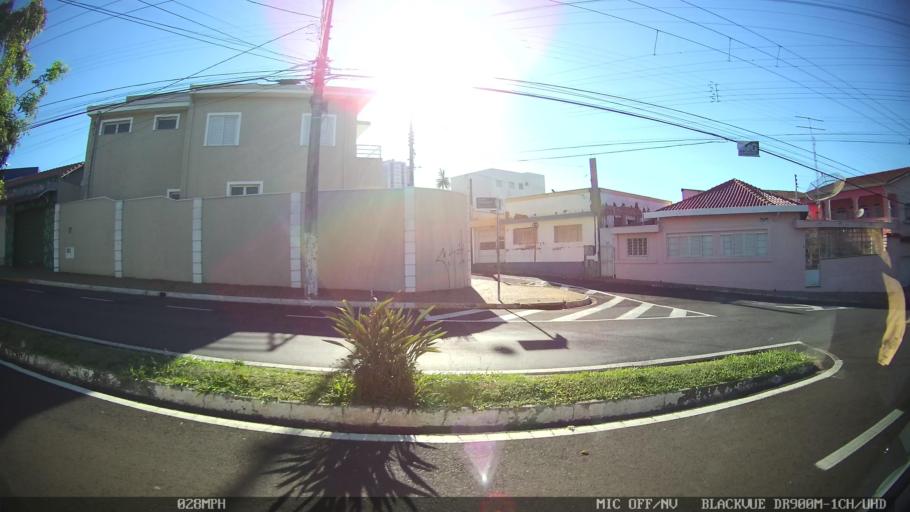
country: BR
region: Sao Paulo
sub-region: Franca
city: Franca
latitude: -20.5448
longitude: -47.4011
